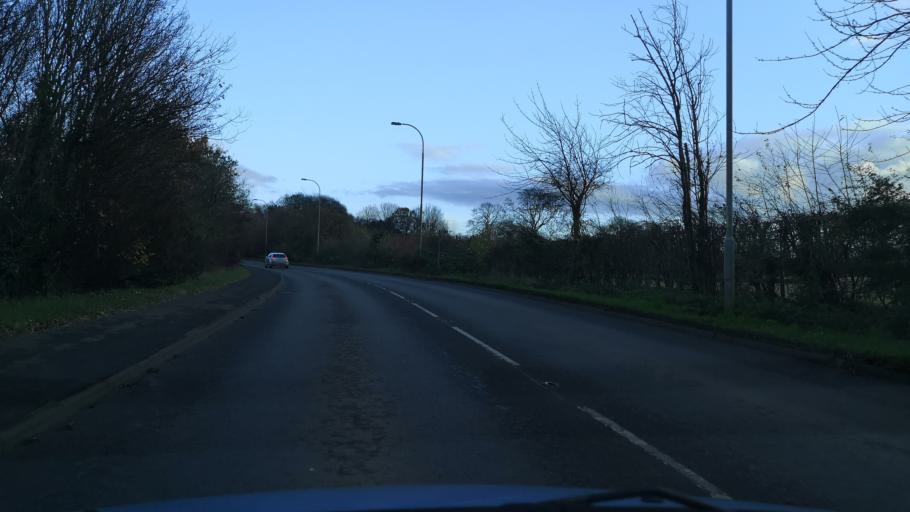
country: GB
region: England
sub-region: City and Borough of Wakefield
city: Crofton
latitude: 53.6598
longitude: -1.4212
